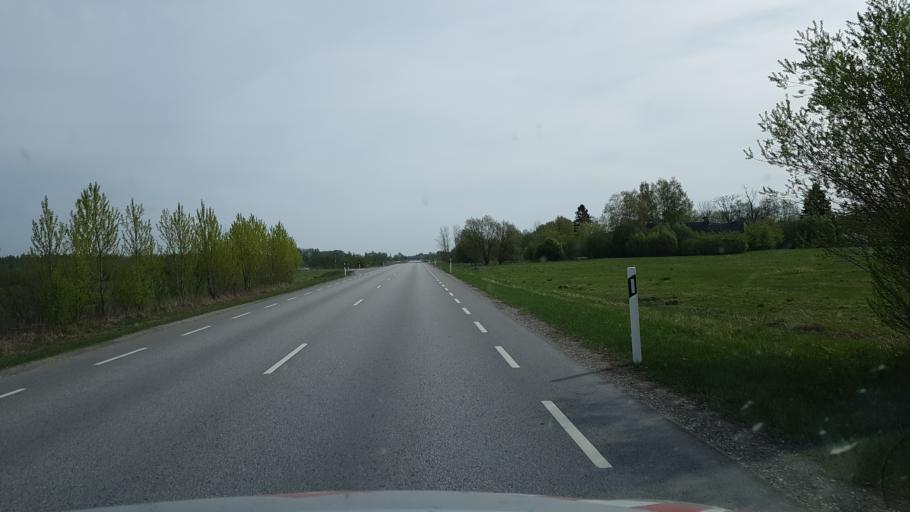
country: EE
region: Paernumaa
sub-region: Sauga vald
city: Sauga
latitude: 58.4450
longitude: 24.4793
